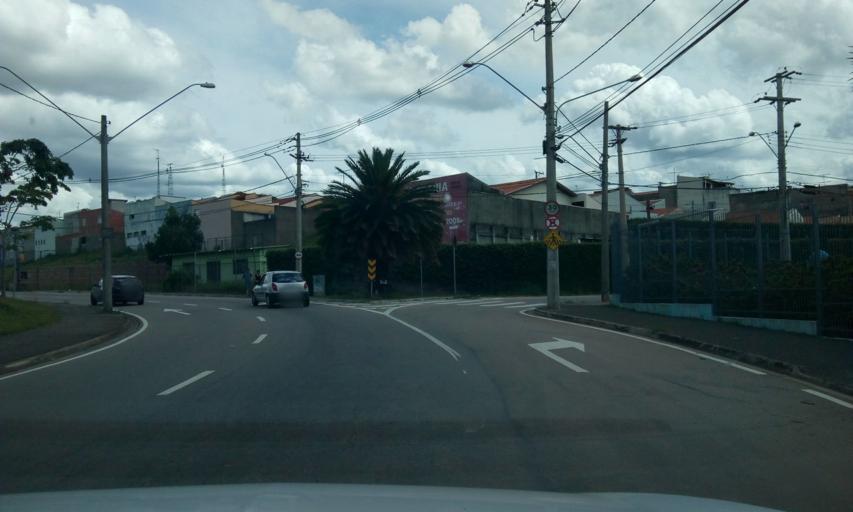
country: BR
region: Sao Paulo
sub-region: Jundiai
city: Jundiai
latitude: -23.1639
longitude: -46.8981
